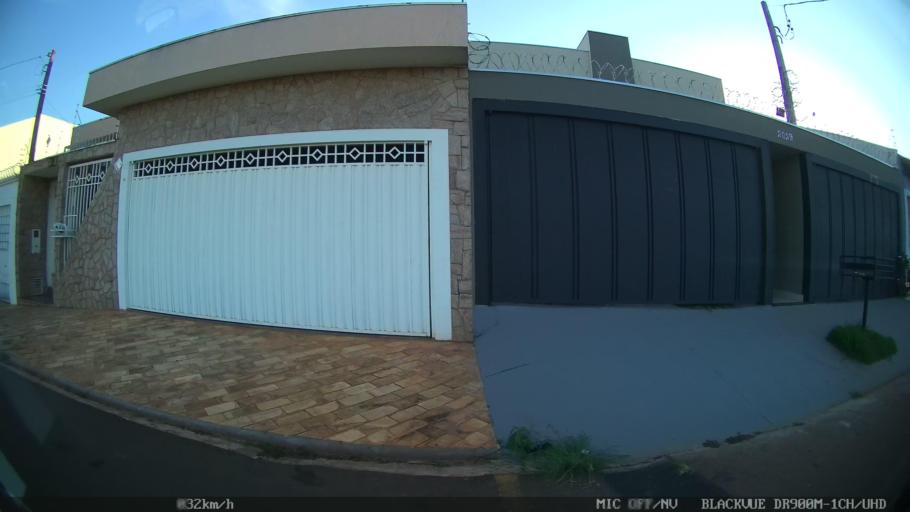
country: BR
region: Sao Paulo
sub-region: Franca
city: Franca
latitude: -20.5146
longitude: -47.3965
